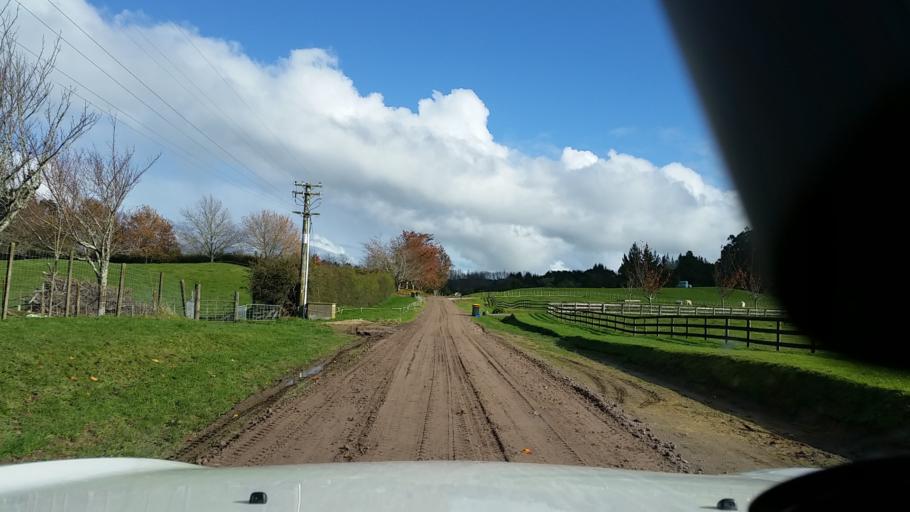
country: NZ
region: Bay of Plenty
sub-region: Rotorua District
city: Rotorua
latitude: -38.0375
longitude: 176.1946
